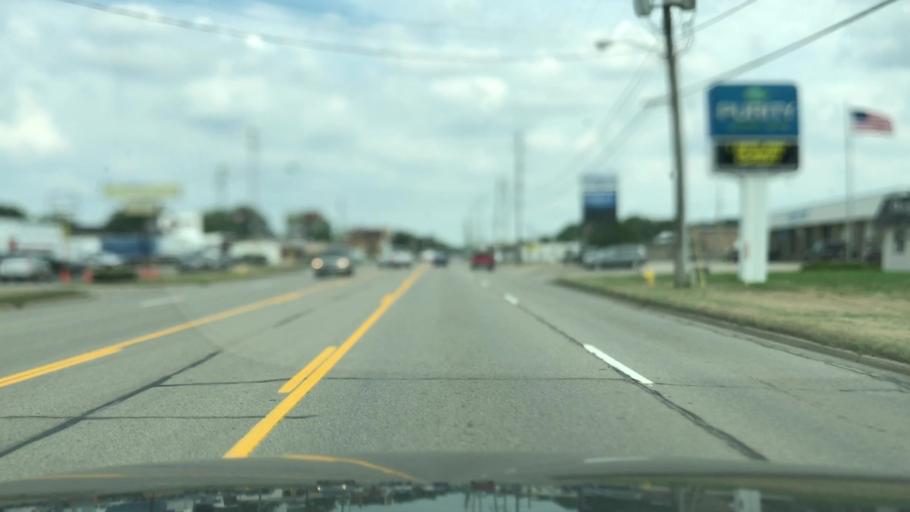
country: US
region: Michigan
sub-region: Kent County
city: Wyoming
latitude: 42.9138
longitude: -85.7296
